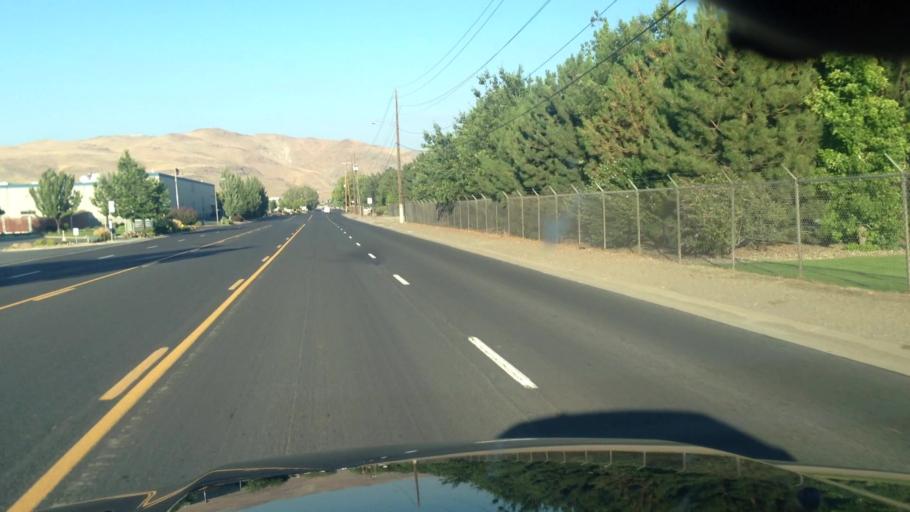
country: US
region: Nevada
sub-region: Washoe County
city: Sparks
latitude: 39.5213
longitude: -119.7279
